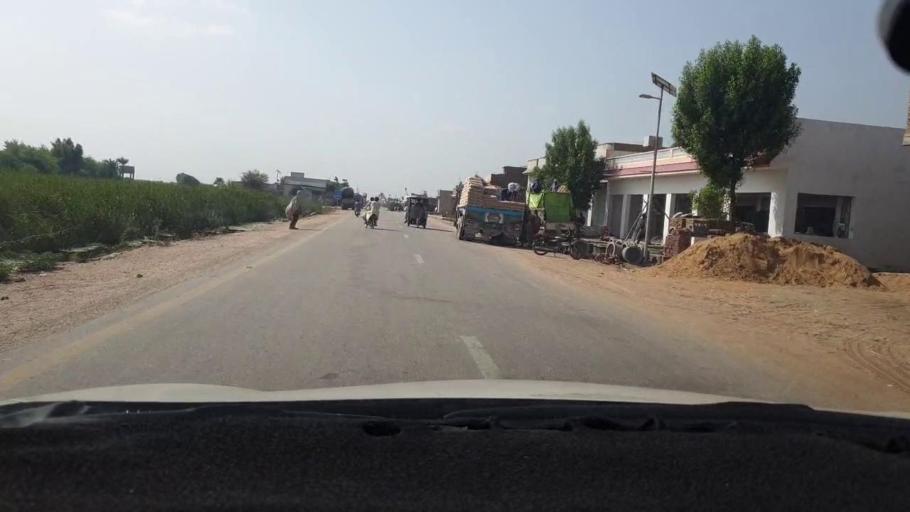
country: PK
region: Sindh
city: Tando Mittha Khan
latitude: 25.7993
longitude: 69.0720
